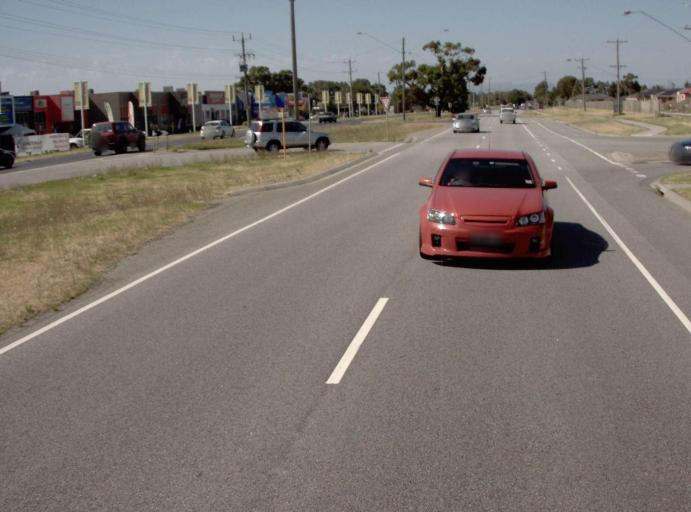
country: AU
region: Victoria
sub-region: Frankston
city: Carrum Downs
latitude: -38.0883
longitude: 145.1816
